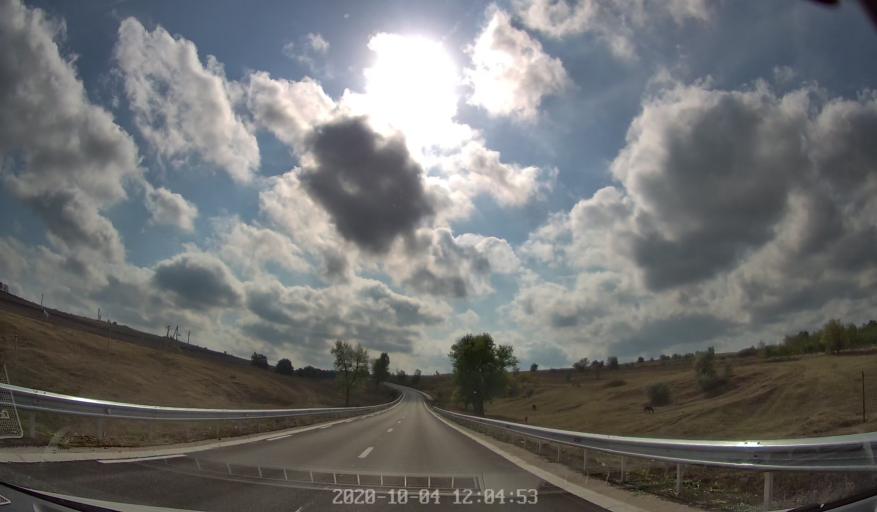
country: MD
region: Rezina
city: Saharna
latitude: 47.5998
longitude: 28.9475
